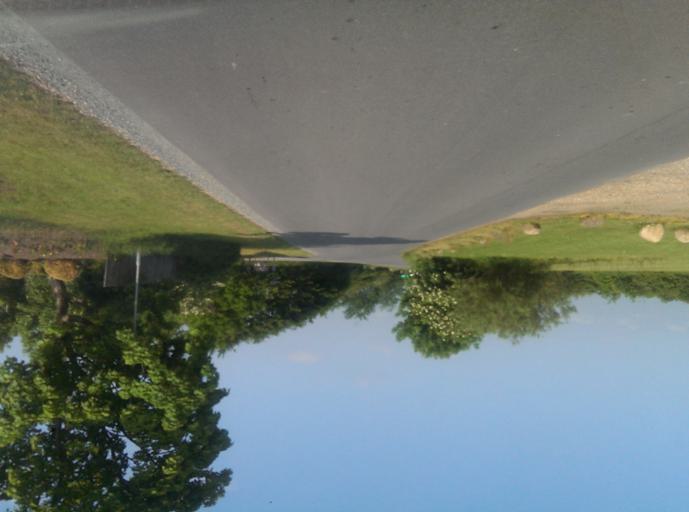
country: DK
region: South Denmark
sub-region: Esbjerg Kommune
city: Tjaereborg
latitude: 55.4485
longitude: 8.6138
